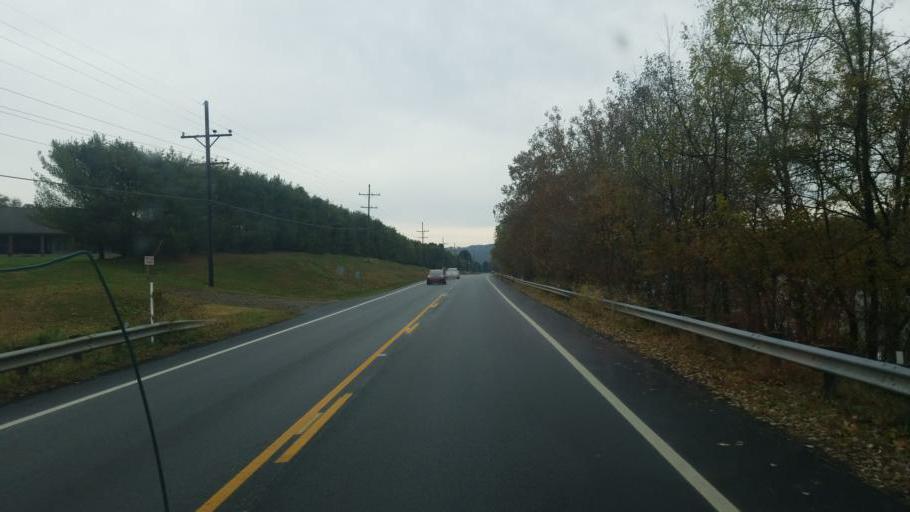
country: US
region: Ohio
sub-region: Washington County
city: Beverly
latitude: 39.5541
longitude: -81.6123
